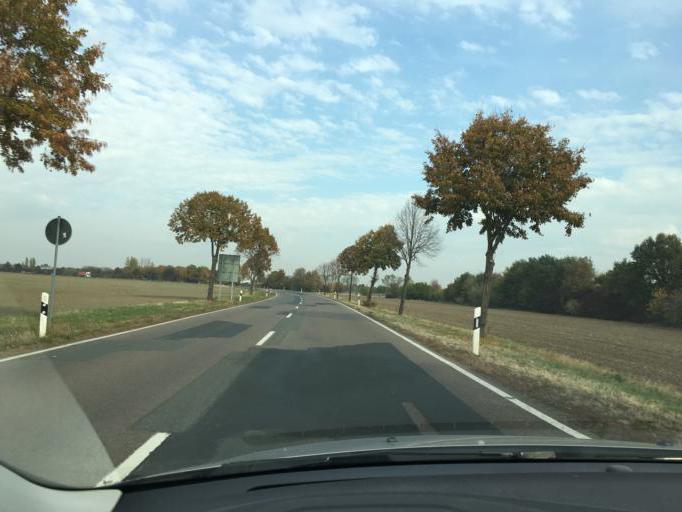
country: DE
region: Saxony
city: Zwochau
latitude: 51.4679
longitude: 12.2690
